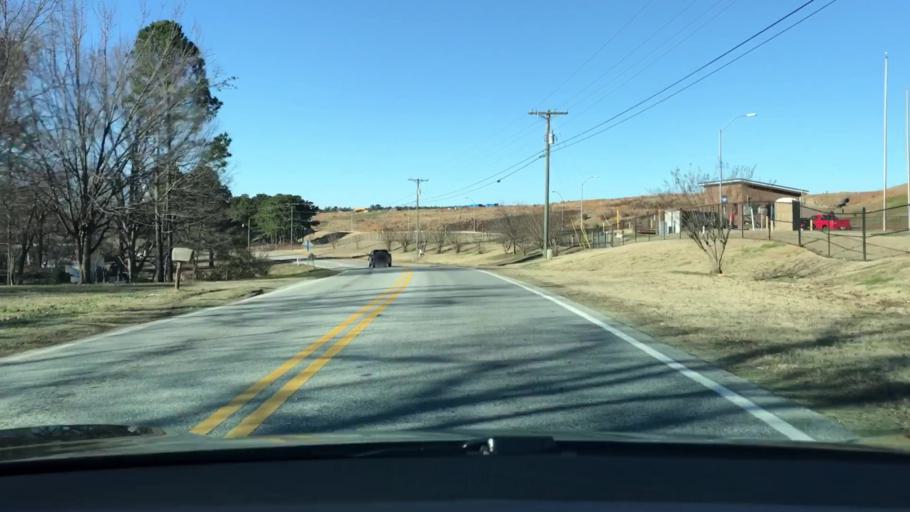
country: US
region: Georgia
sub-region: Barrow County
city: Winder
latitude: 33.9658
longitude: -83.7733
